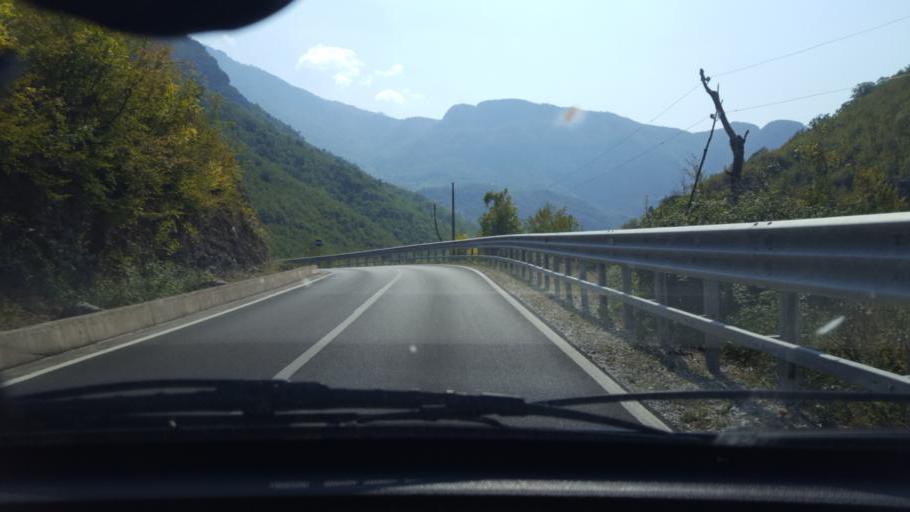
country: AL
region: Shkoder
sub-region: Rrethi i Malesia e Madhe
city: Kastrat
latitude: 42.4402
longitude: 19.5384
